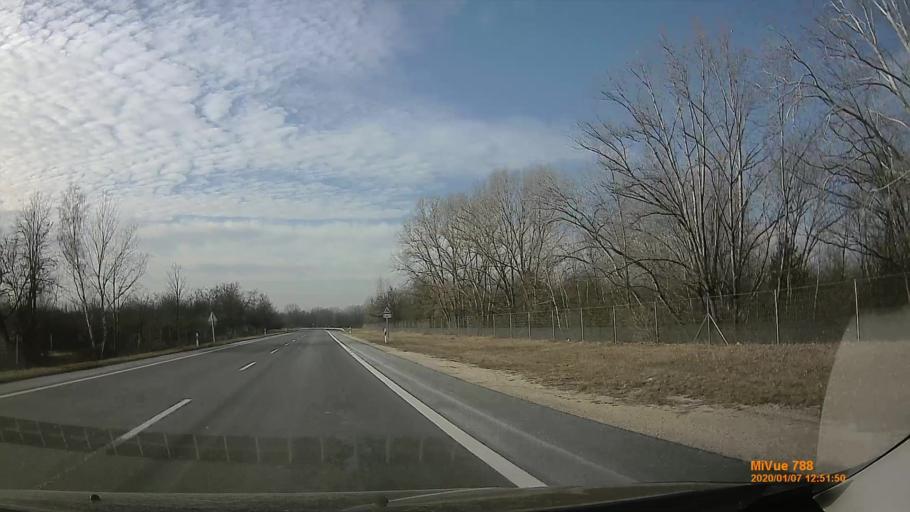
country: HU
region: Gyor-Moson-Sopron
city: Gyor
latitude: 47.7162
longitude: 17.6923
